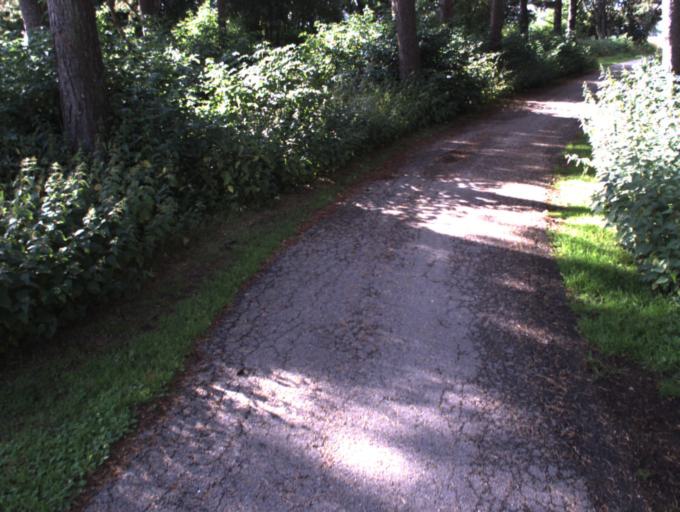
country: SE
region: Skane
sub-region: Helsingborg
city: Odakra
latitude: 56.0741
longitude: 12.7226
